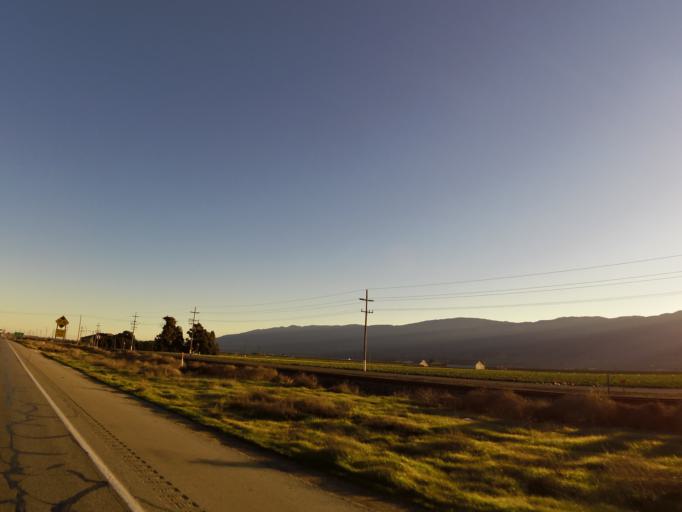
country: US
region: California
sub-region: Monterey County
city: Gonzales
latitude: 36.5316
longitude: -121.4758
